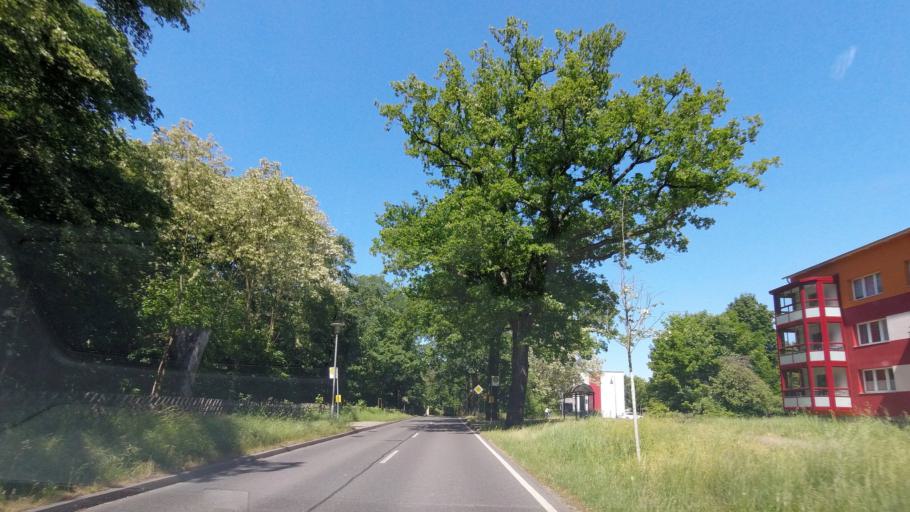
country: DE
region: Brandenburg
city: Ludwigsfelde
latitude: 52.2874
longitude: 13.2106
